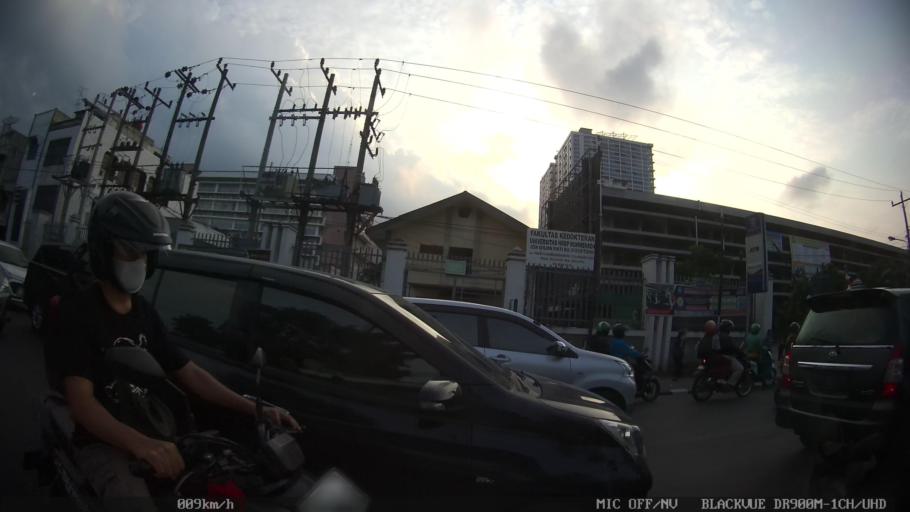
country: ID
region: North Sumatra
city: Medan
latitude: 3.5966
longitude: 98.6821
